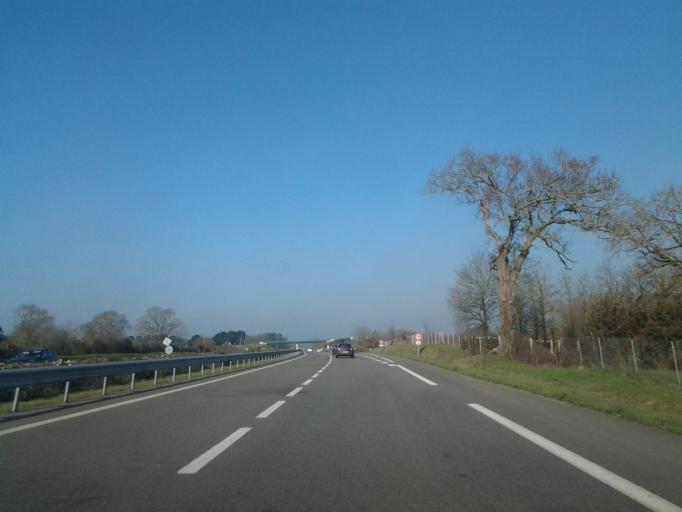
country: FR
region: Pays de la Loire
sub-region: Departement de la Vendee
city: Saint-Christophe-du-Ligneron
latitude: 46.7998
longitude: -1.7245
